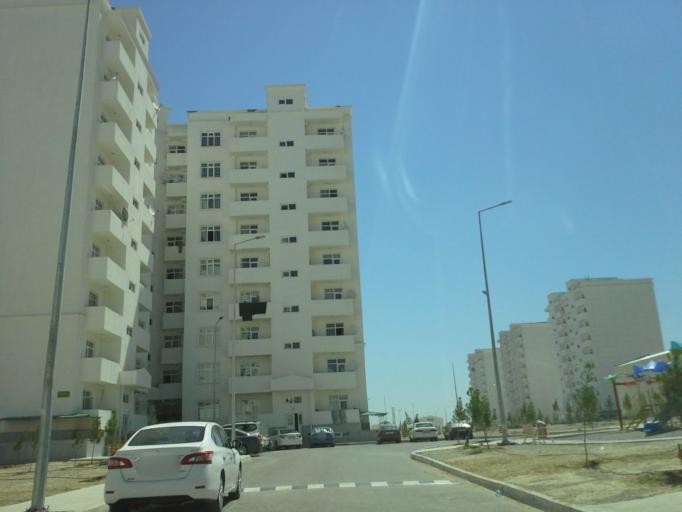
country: TM
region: Ahal
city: Ashgabat
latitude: 37.8893
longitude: 58.4083
